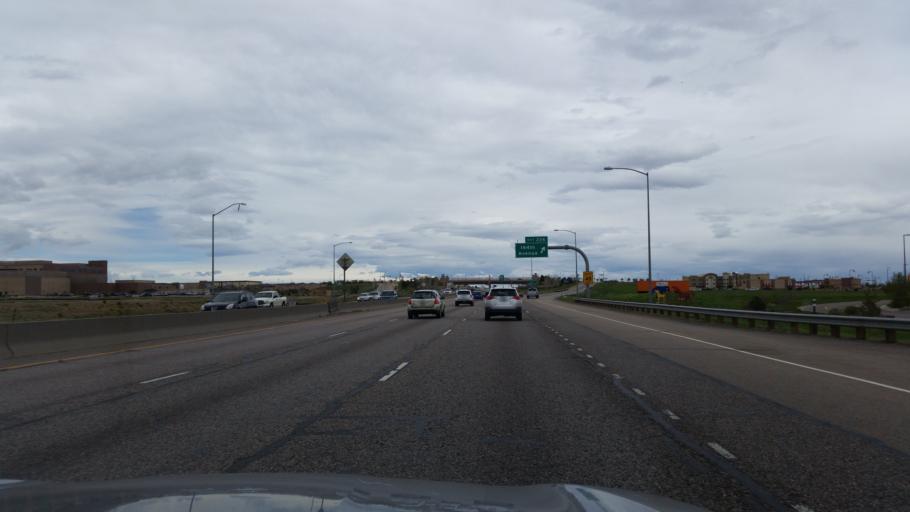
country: US
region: Colorado
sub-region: Adams County
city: Northglenn
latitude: 39.9511
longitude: -104.9877
